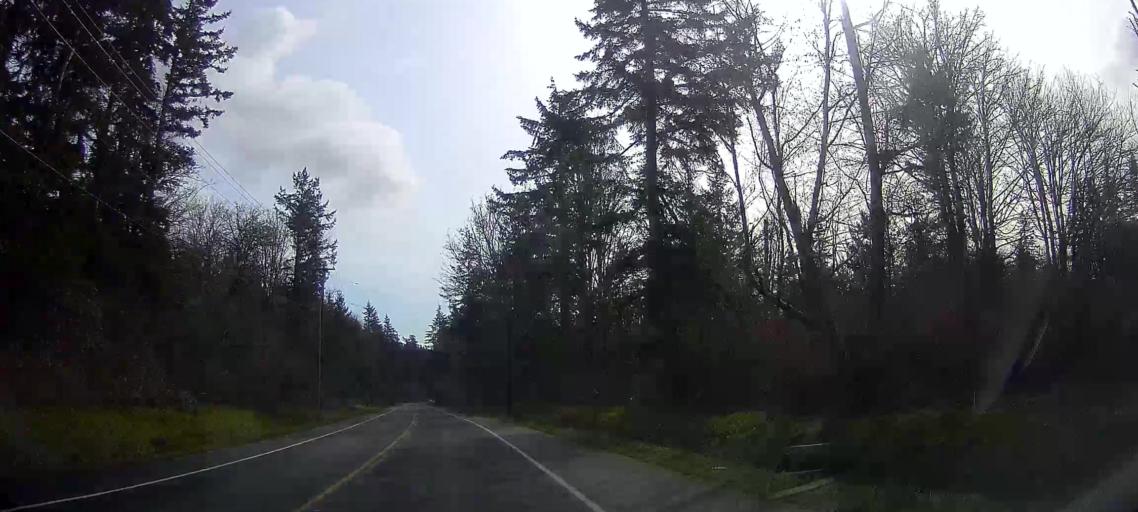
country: US
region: Washington
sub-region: Island County
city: Camano
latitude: 48.1519
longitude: -122.4745
